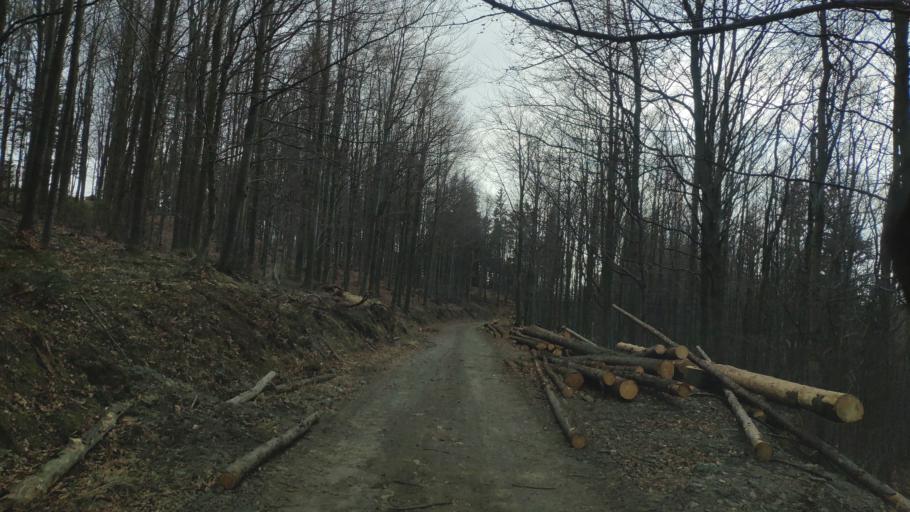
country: SK
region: Kosicky
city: Moldava nad Bodvou
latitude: 48.7496
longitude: 21.0410
